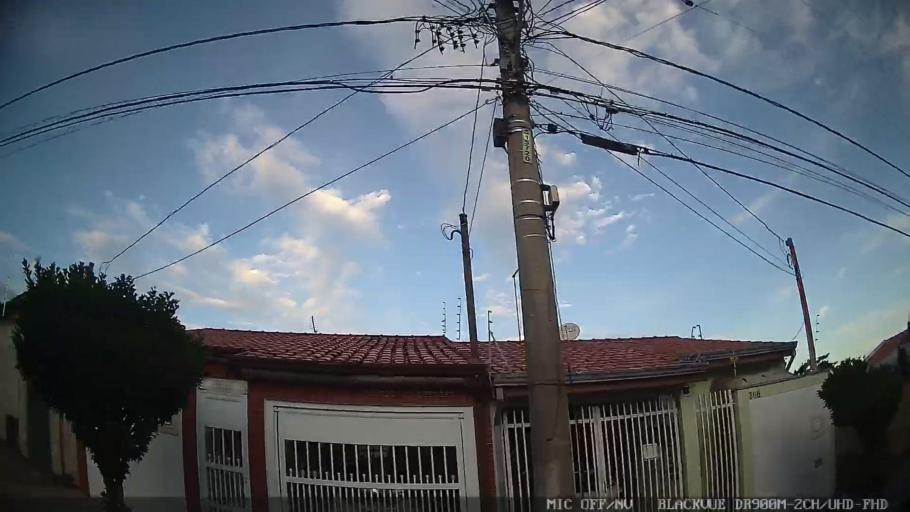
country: BR
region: Sao Paulo
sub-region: Salto
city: Salto
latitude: -23.1968
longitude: -47.2858
